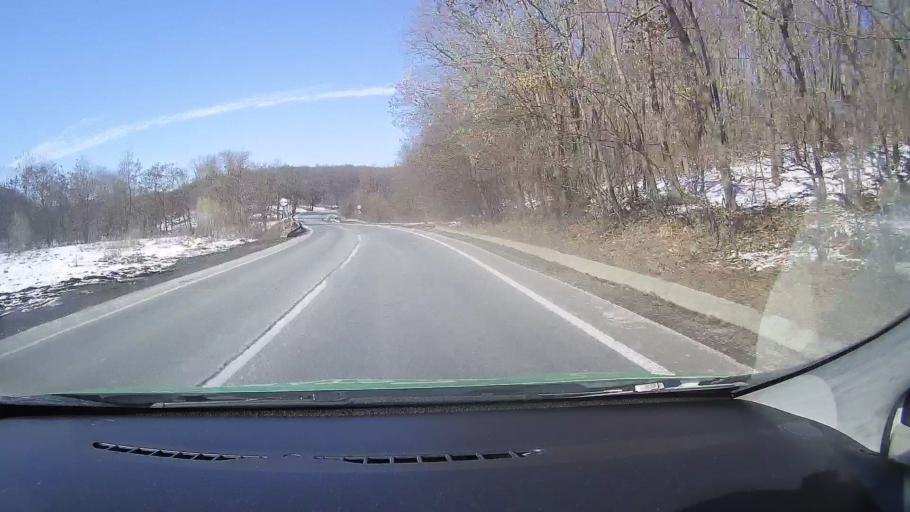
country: RO
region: Brasov
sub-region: Oras Rupea
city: Fiser
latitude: 46.0828
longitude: 25.1277
